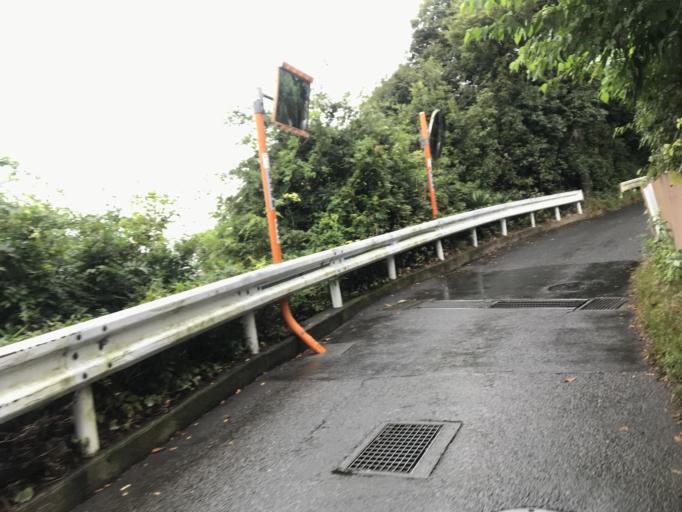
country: JP
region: Kanagawa
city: Zama
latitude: 35.5491
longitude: 139.3249
